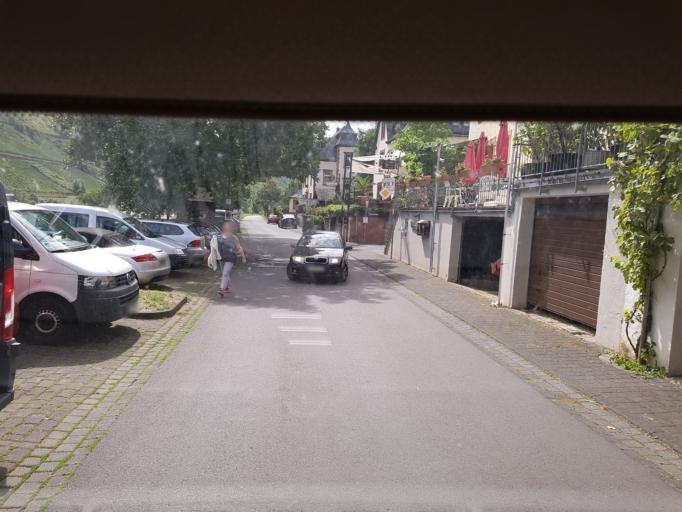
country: DE
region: Rheinland-Pfalz
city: Reil
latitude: 50.0197
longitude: 7.1189
